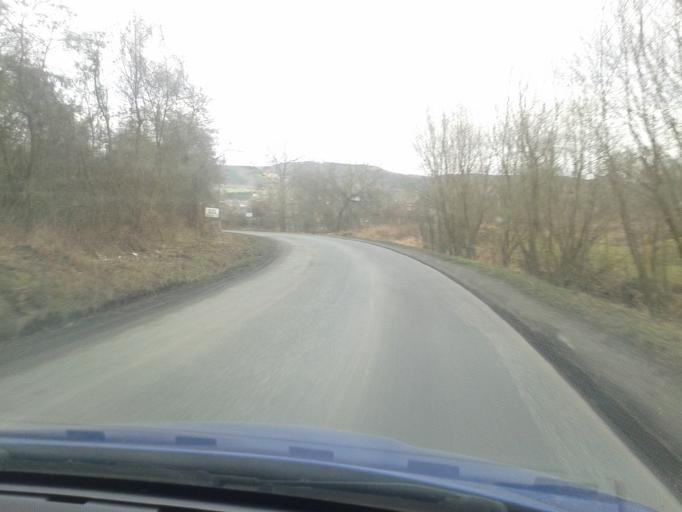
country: CZ
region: Central Bohemia
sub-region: Okres Beroun
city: Kraluv Dvur
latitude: 49.9400
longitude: 14.0451
